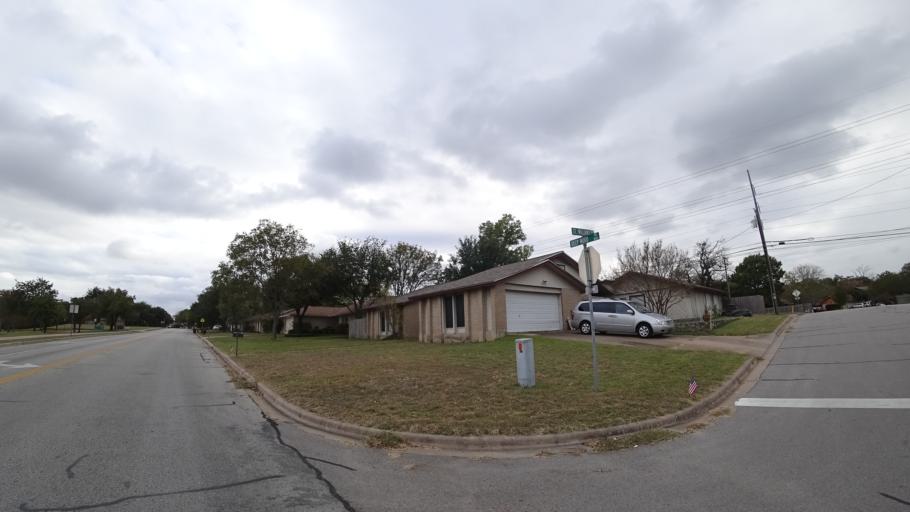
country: US
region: Texas
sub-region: Williamson County
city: Round Rock
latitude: 30.5006
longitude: -97.6983
